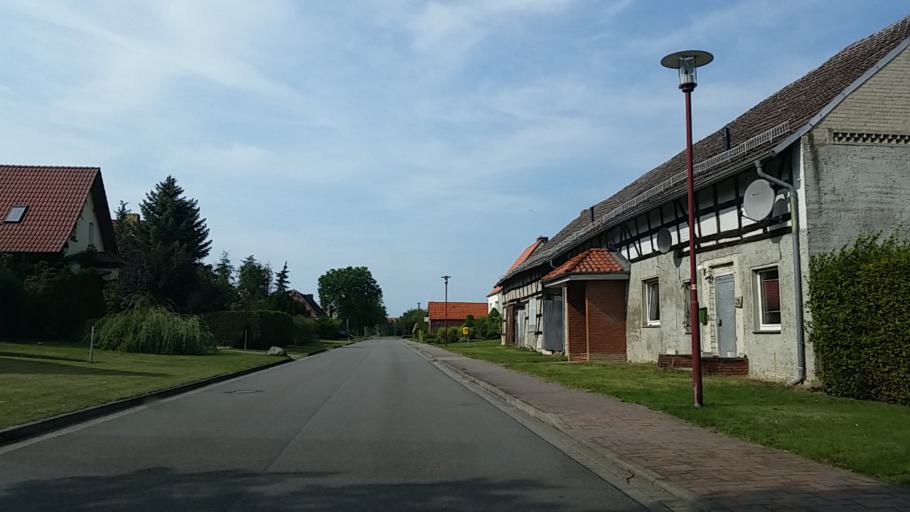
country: DE
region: Saxony-Anhalt
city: Salzwedel
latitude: 52.8442
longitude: 11.1207
